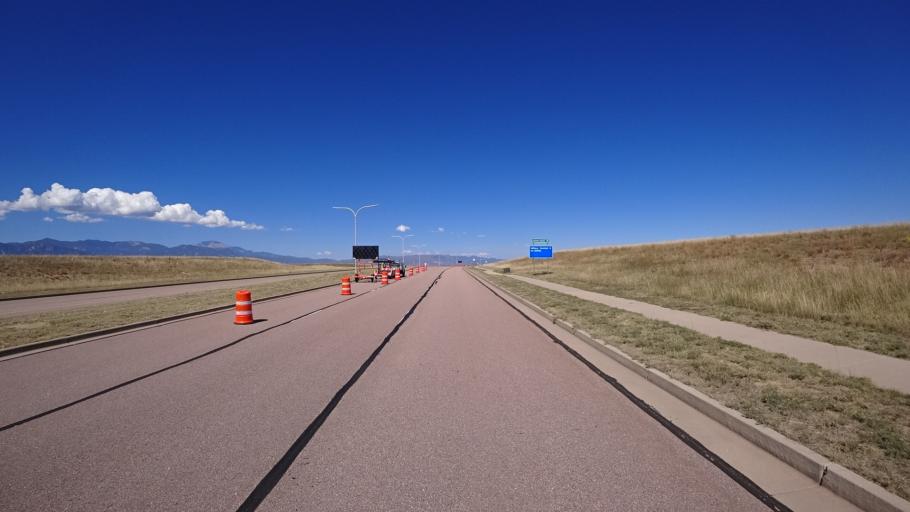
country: US
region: Colorado
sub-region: El Paso County
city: Security-Widefield
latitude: 38.7729
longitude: -104.7014
